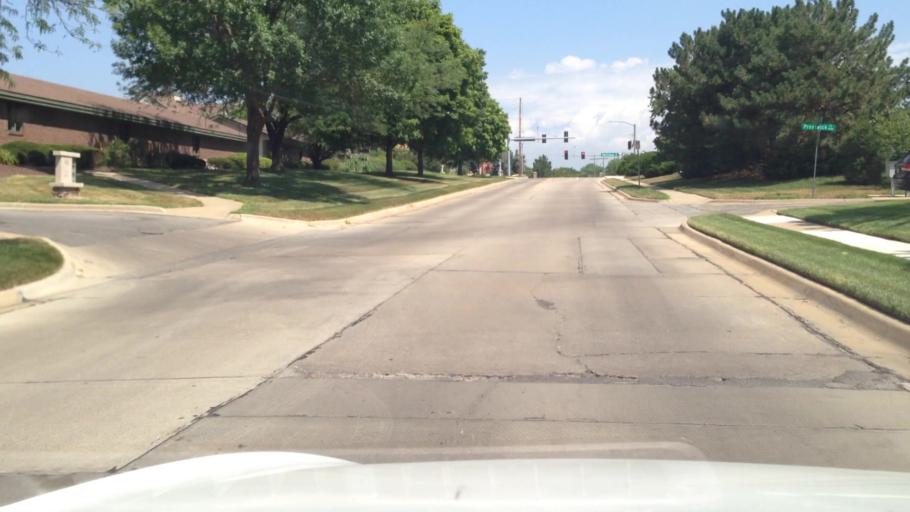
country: US
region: Kansas
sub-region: Douglas County
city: Lawrence
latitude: 38.9555
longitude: -95.3022
